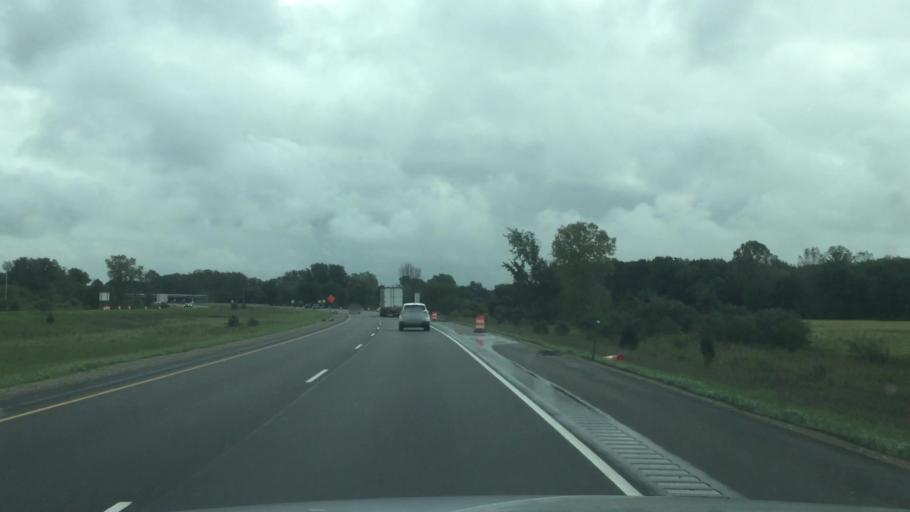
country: US
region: Michigan
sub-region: Ingham County
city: Webberville
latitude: 42.6537
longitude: -84.1877
